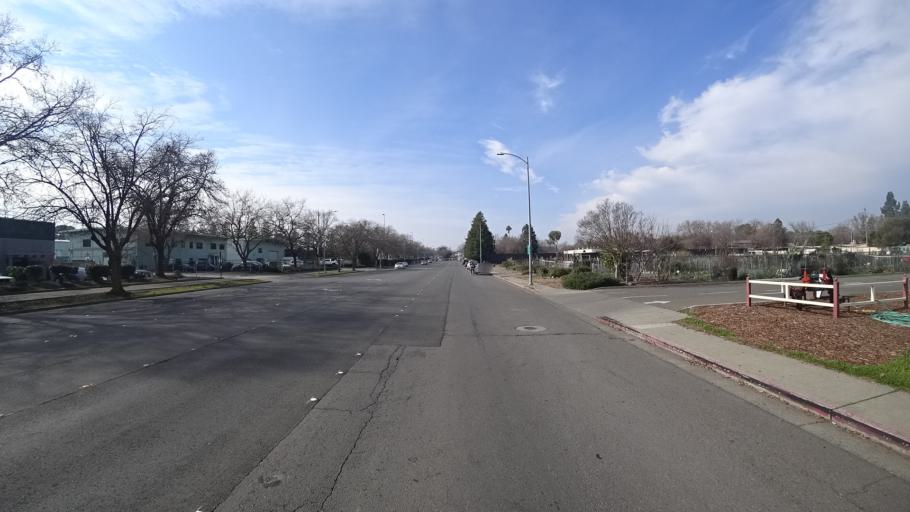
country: US
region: California
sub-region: Yolo County
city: Davis
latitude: 38.5489
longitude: -121.7285
